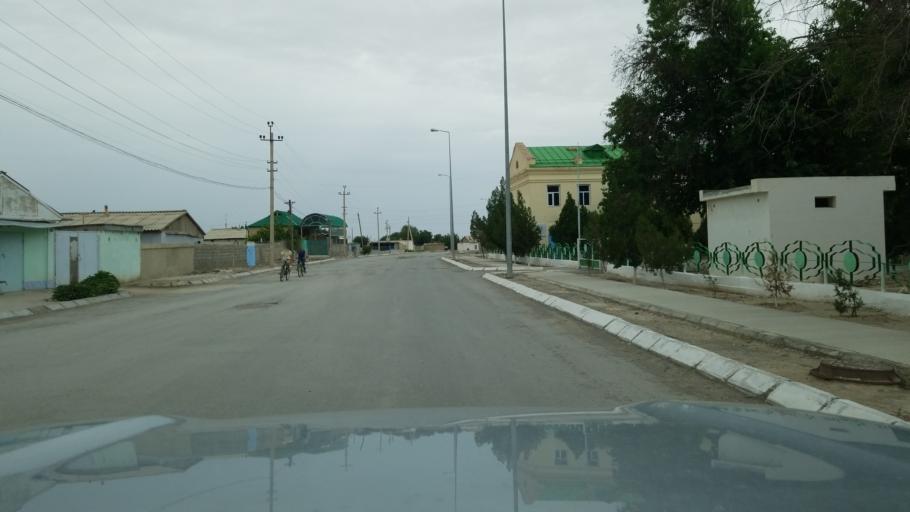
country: TM
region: Balkan
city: Serdar
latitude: 38.9850
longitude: 56.2755
